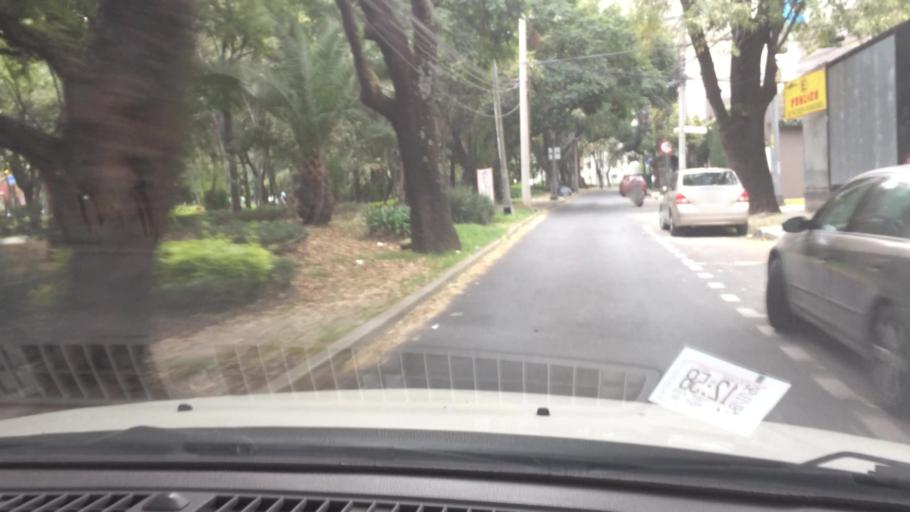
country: MX
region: Mexico City
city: Coyoacan
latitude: 19.3516
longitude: -99.1828
